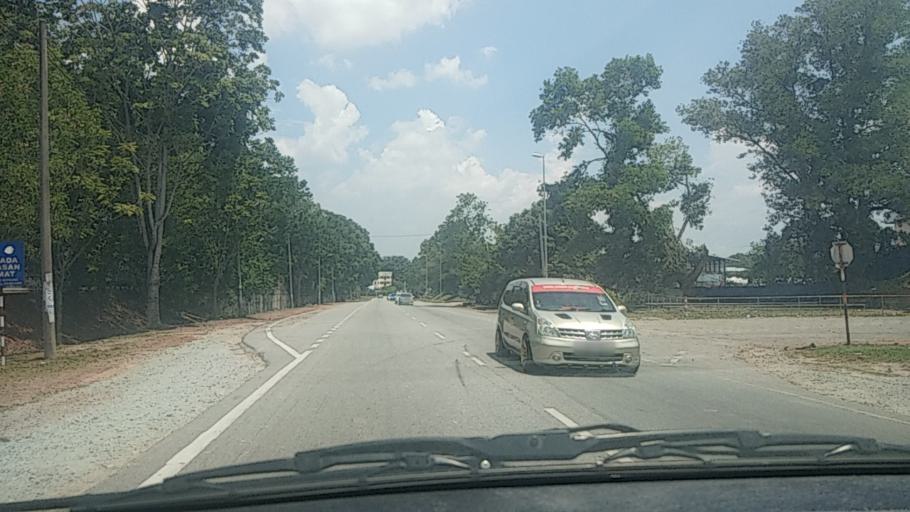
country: MY
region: Kedah
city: Sungai Petani
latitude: 5.6466
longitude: 100.5362
